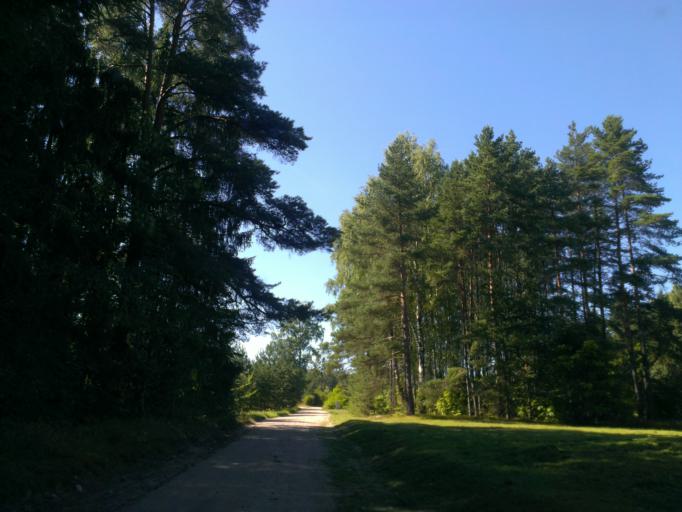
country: LV
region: Sigulda
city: Sigulda
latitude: 57.1026
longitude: 24.8186
